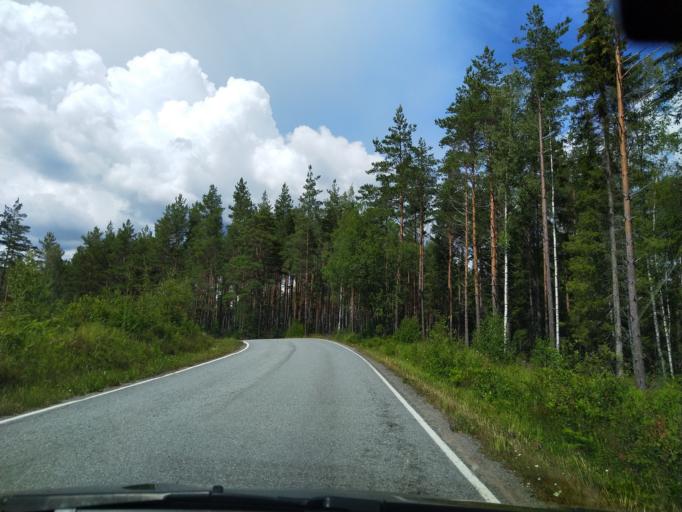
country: FI
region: Uusimaa
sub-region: Raaseporin
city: Karis
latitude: 59.9970
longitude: 23.6839
